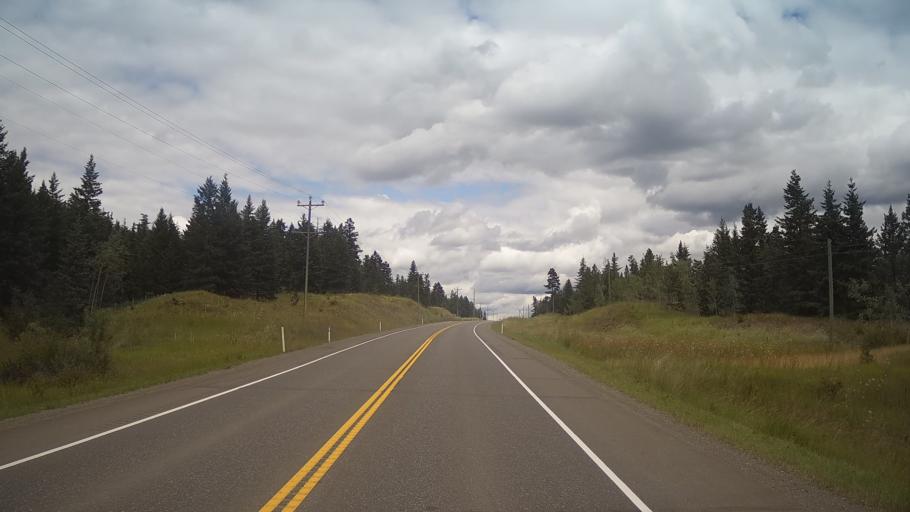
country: CA
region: British Columbia
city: Cache Creek
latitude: 51.1535
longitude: -121.5034
